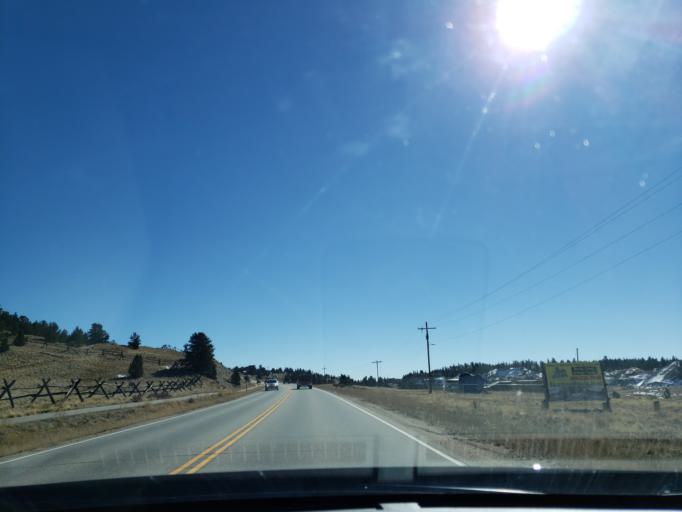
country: US
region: Colorado
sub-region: Park County
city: Fairplay
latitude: 39.2351
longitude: -106.0236
